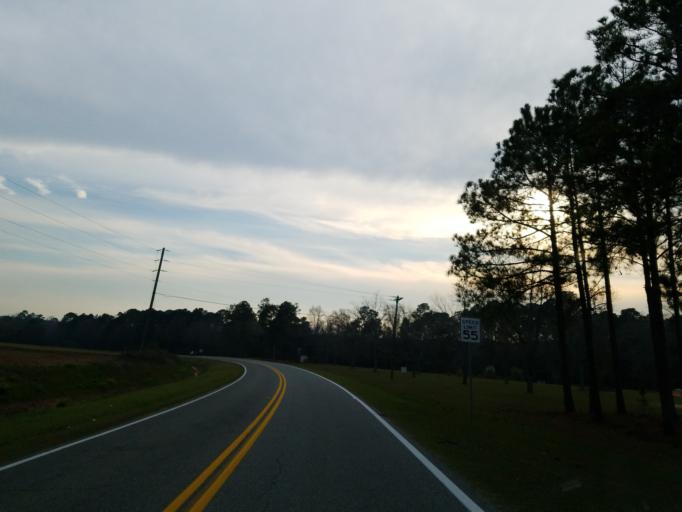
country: US
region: Georgia
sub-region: Tift County
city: Unionville
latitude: 31.4358
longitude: -83.5686
